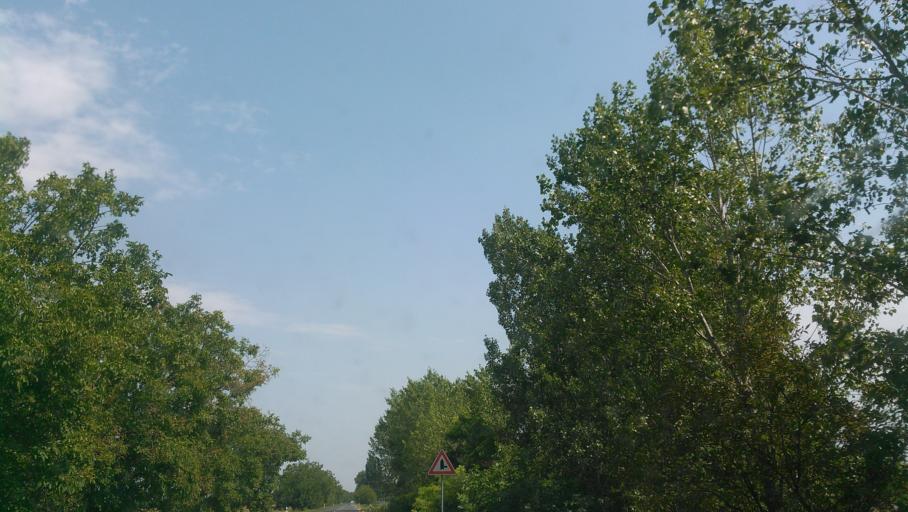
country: SK
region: Trnavsky
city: Dunajska Streda
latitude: 48.0425
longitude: 17.5068
